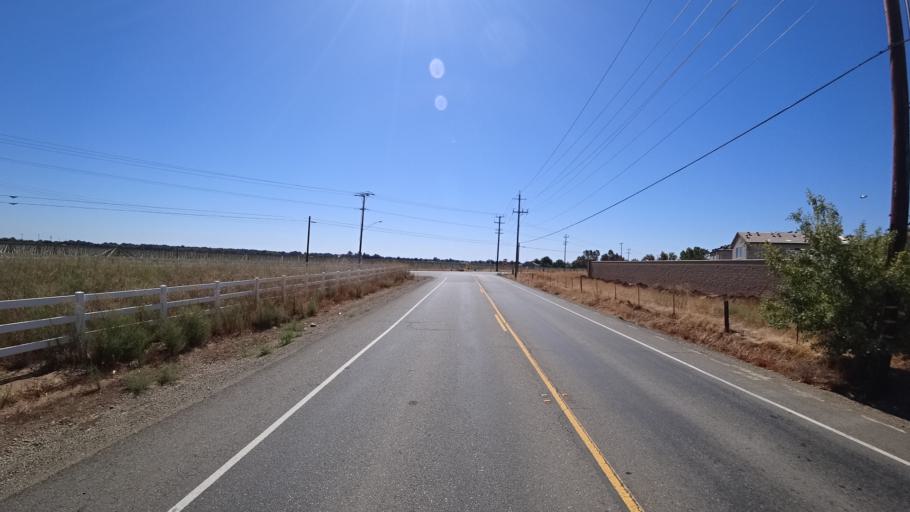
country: US
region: California
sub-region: Sacramento County
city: Elk Grove
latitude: 38.4003
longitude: -121.3347
